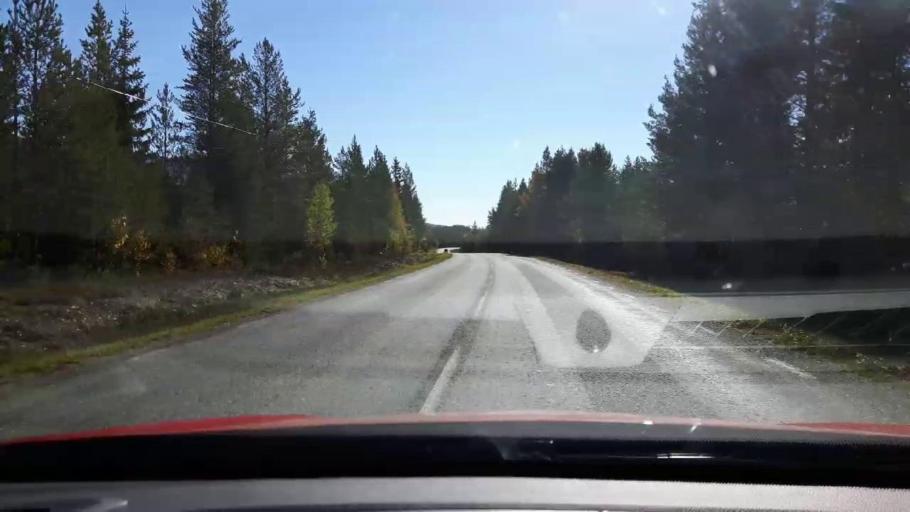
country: SE
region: Jaemtland
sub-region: Harjedalens Kommun
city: Sveg
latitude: 62.4328
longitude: 13.8844
